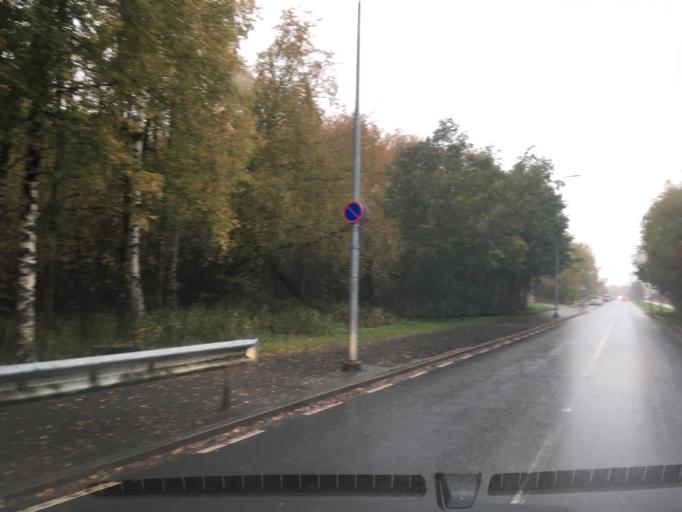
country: EE
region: Harju
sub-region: Tallinna linn
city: Kose
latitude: 59.4546
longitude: 24.8508
